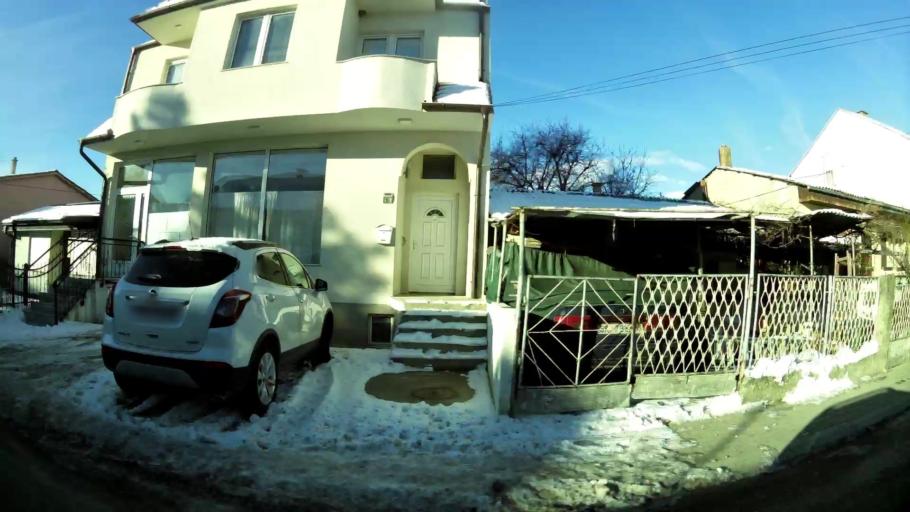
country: MK
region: Saraj
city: Saraj
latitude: 42.0084
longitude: 21.3334
